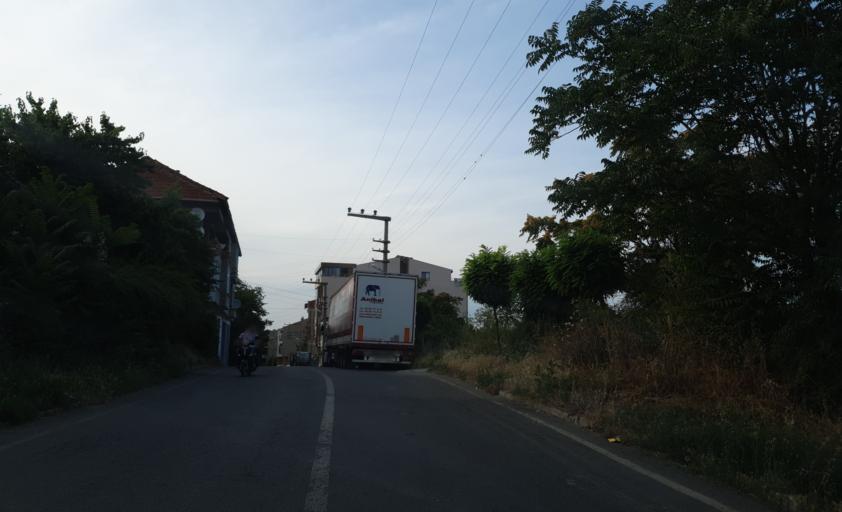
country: TR
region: Tekirdag
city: Hayrabolu
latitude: 41.2137
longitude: 27.1104
